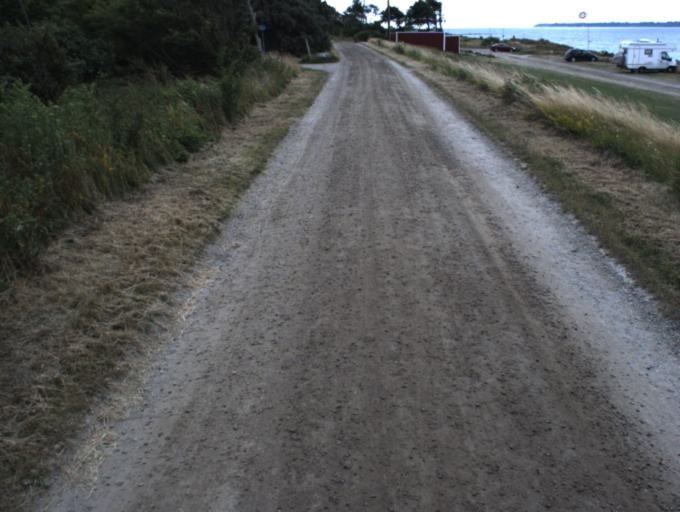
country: SE
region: Skane
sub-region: Helsingborg
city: Rydeback
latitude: 55.9640
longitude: 12.7585
